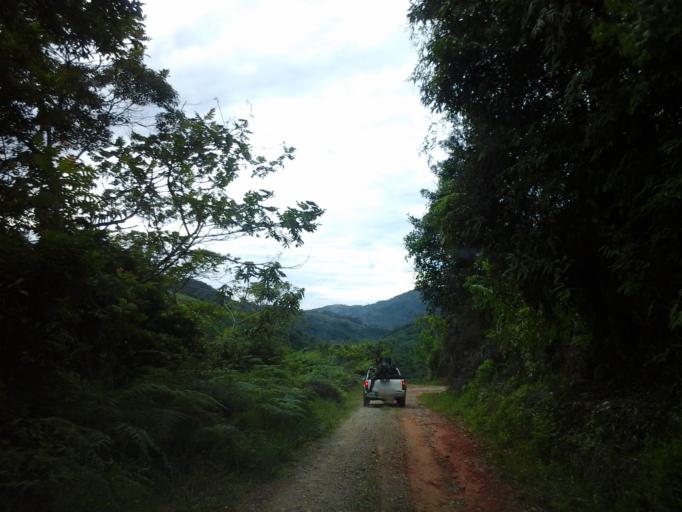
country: CO
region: Antioquia
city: San Roque
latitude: 6.4976
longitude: -74.9702
